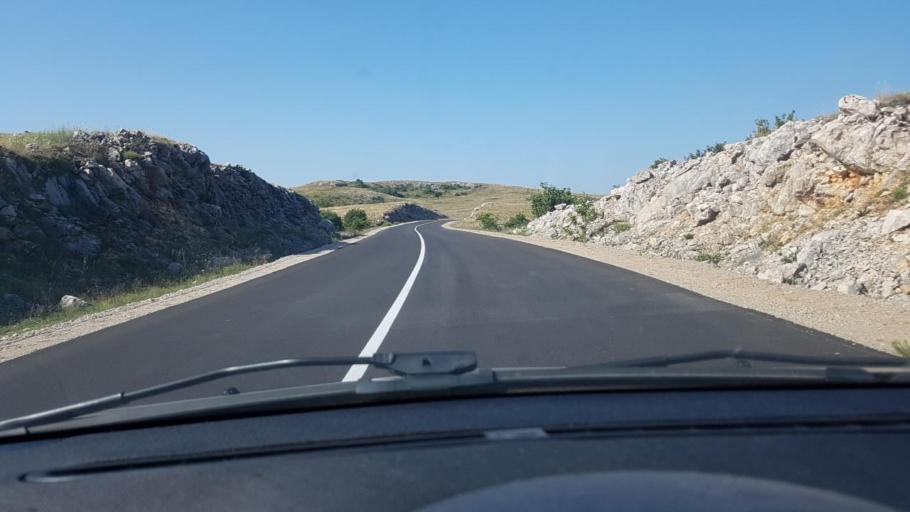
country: BA
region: Federation of Bosnia and Herzegovina
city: Tomislavgrad
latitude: 43.7925
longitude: 17.2561
